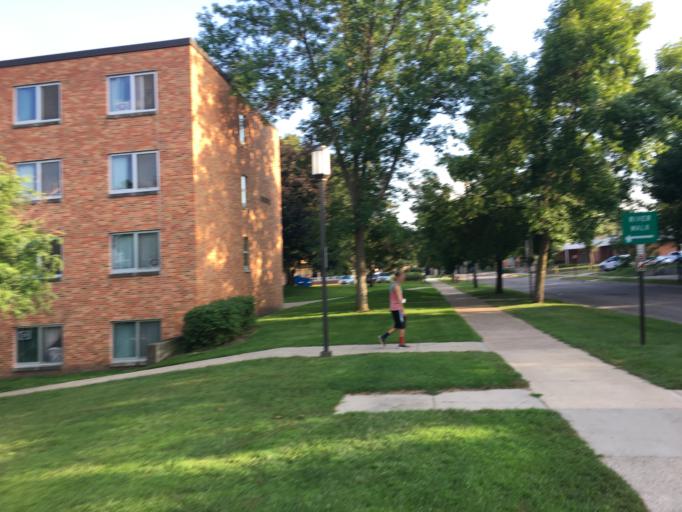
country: US
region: Minnesota
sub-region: Stearns County
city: Saint Cloud
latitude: 45.5554
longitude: -94.1489
